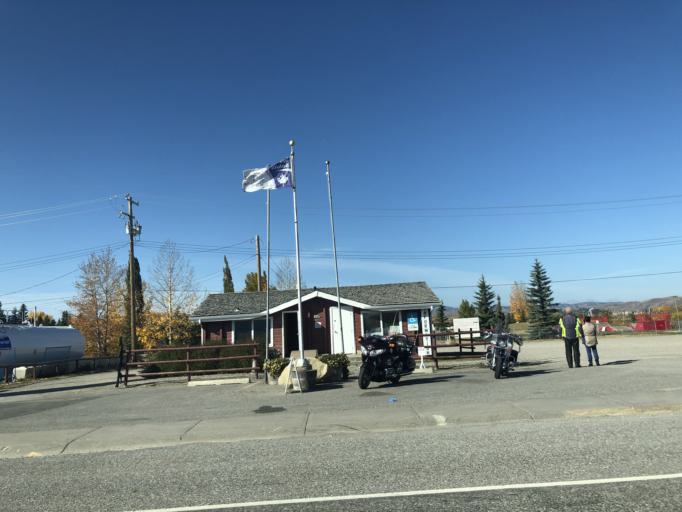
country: CA
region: Alberta
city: Black Diamond
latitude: 50.5343
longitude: -114.2310
